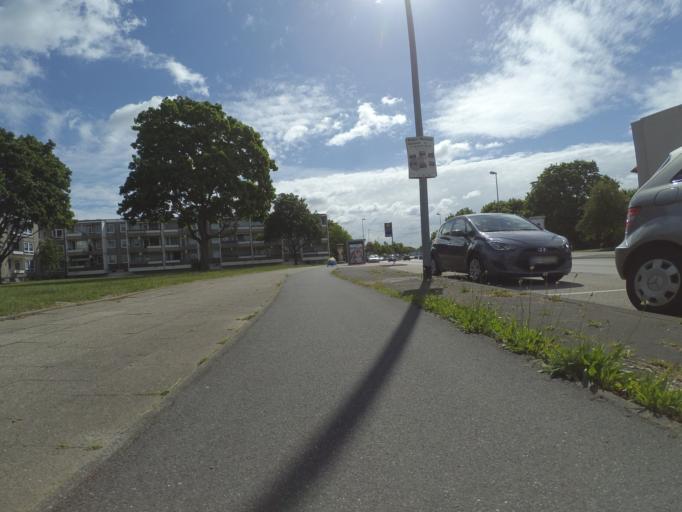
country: DE
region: Lower Saxony
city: Auf der Horst
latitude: 52.4198
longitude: 9.6135
